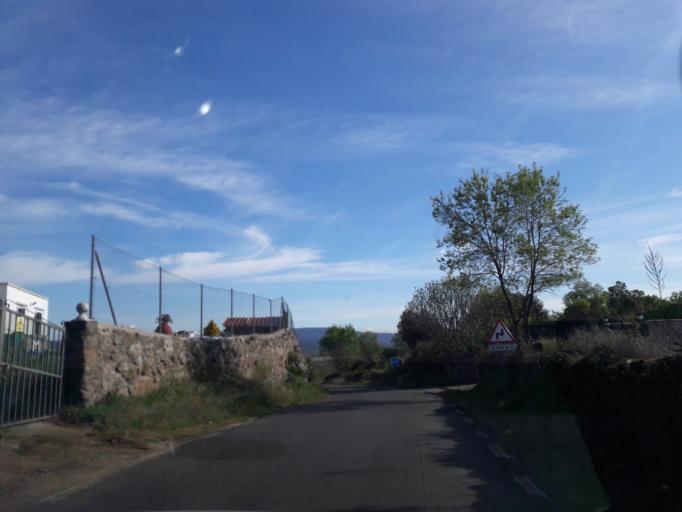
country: ES
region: Castille and Leon
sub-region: Provincia de Salamanca
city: Navalmoral de Bejar
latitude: 40.4271
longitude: -5.7832
